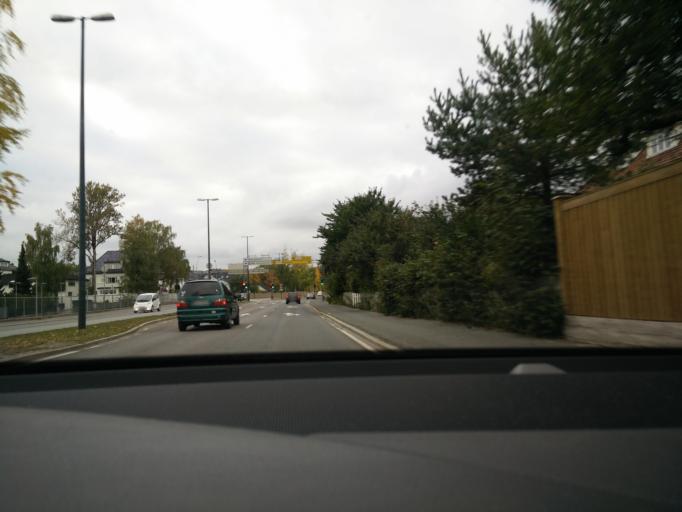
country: NO
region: Oslo
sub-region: Oslo
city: Sjolyststranda
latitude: 59.9349
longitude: 10.6960
